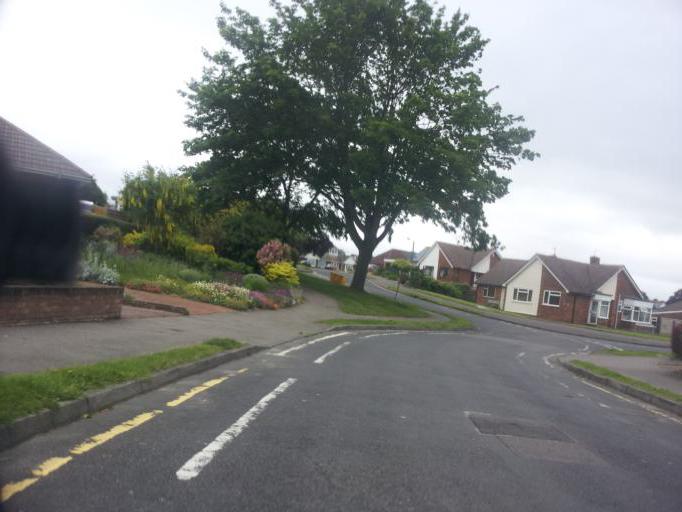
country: GB
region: England
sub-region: Kent
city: Maidstone
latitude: 51.2746
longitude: 0.4963
